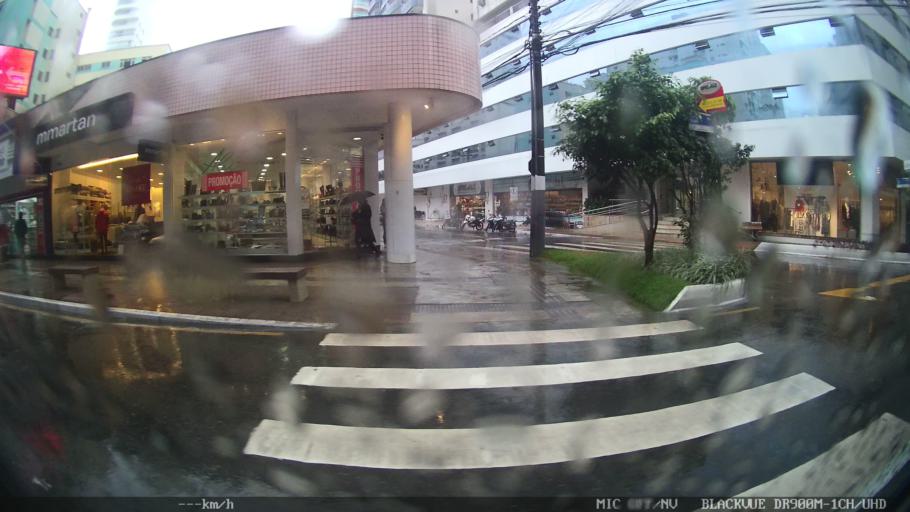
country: BR
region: Santa Catarina
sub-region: Balneario Camboriu
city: Balneario Camboriu
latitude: -26.9854
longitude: -48.6353
